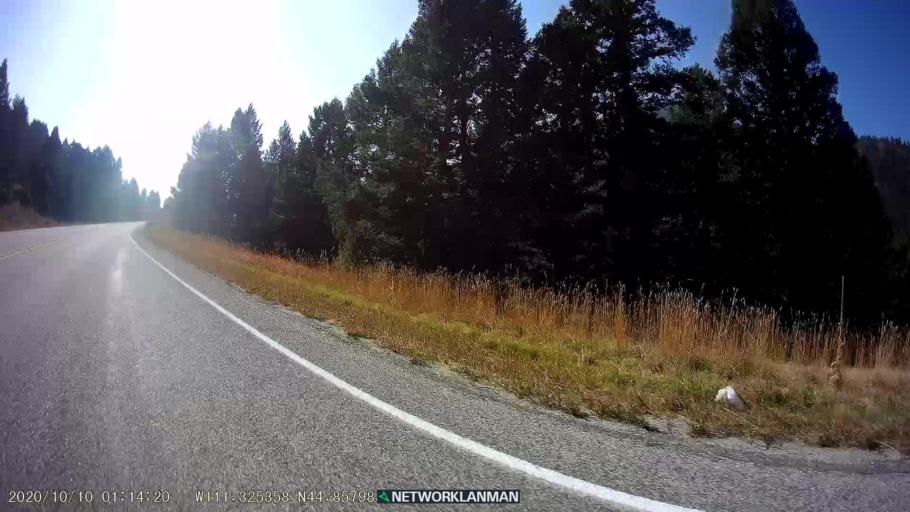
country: US
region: Montana
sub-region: Gallatin County
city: West Yellowstone
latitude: 44.8577
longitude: -111.3250
